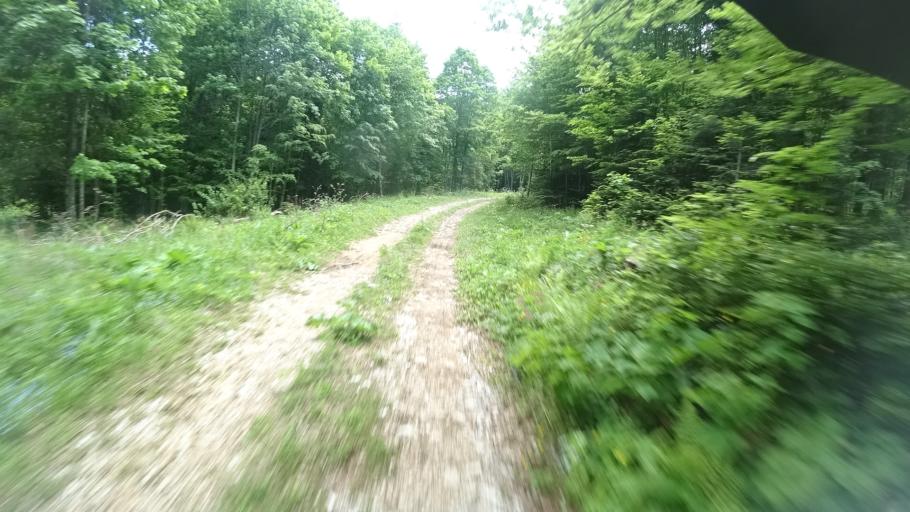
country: HR
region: Zadarska
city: Gracac
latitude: 44.4799
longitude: 15.8826
